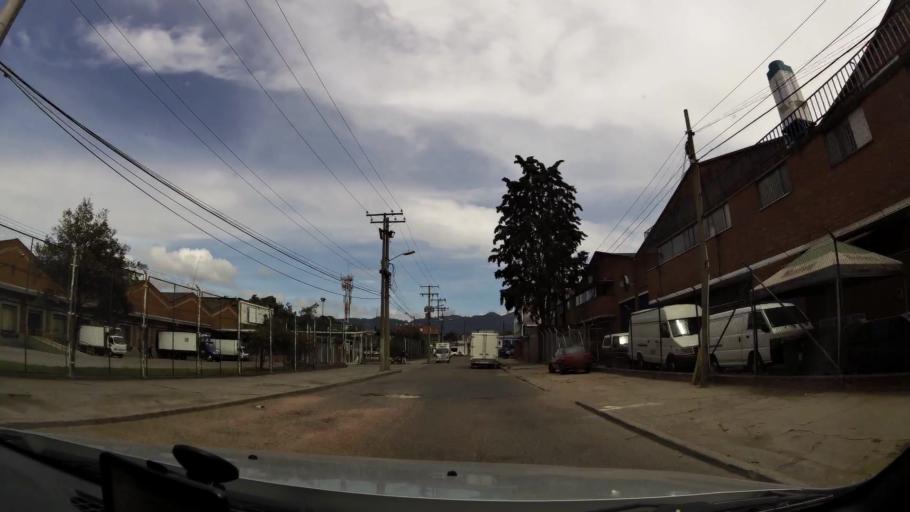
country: CO
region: Bogota D.C.
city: Bogota
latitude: 4.6312
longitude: -74.1228
